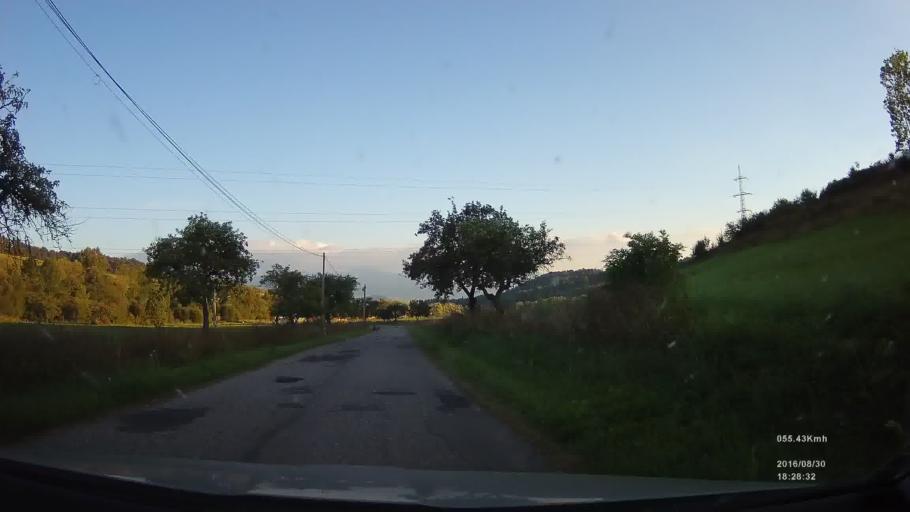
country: SK
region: Zilinsky
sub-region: Okres Liptovsky Mikulas
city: Liptovsky Mikulas
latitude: 49.1402
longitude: 19.5012
